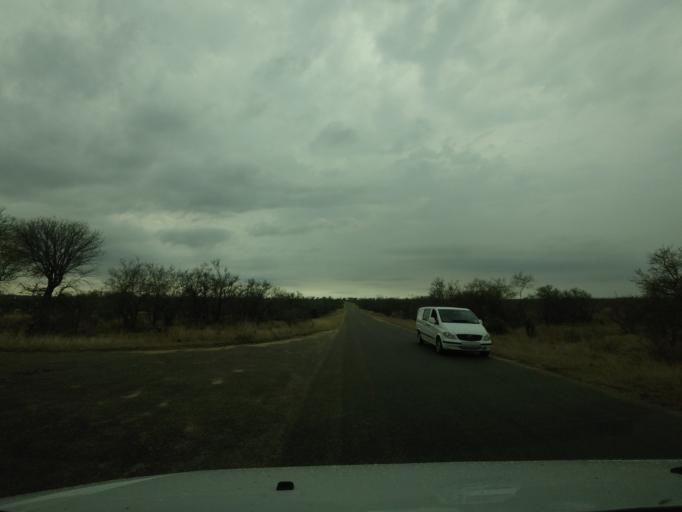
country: ZA
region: Limpopo
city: Thulamahashi
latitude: -24.4758
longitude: 31.3914
